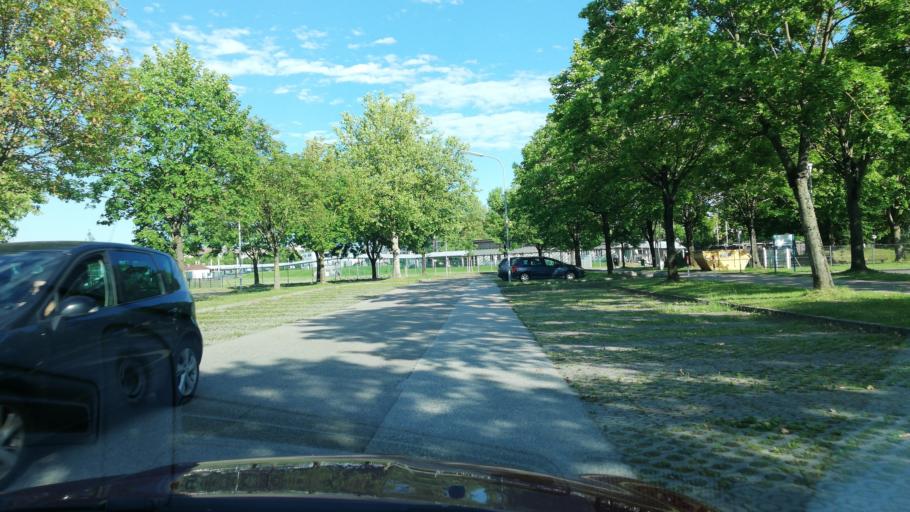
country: AT
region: Upper Austria
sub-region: Politischer Bezirk Linz-Land
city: Leonding
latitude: 48.2678
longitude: 14.2533
